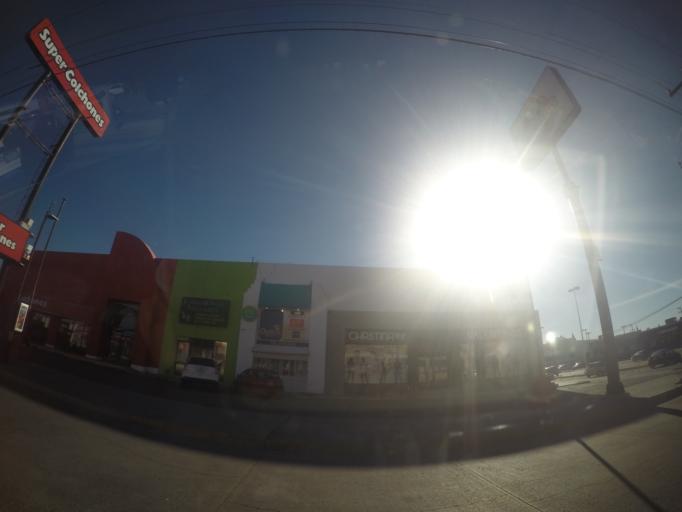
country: MX
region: Chihuahua
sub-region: Chihuahua
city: Chihuahua
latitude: 28.6725
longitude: -106.1019
